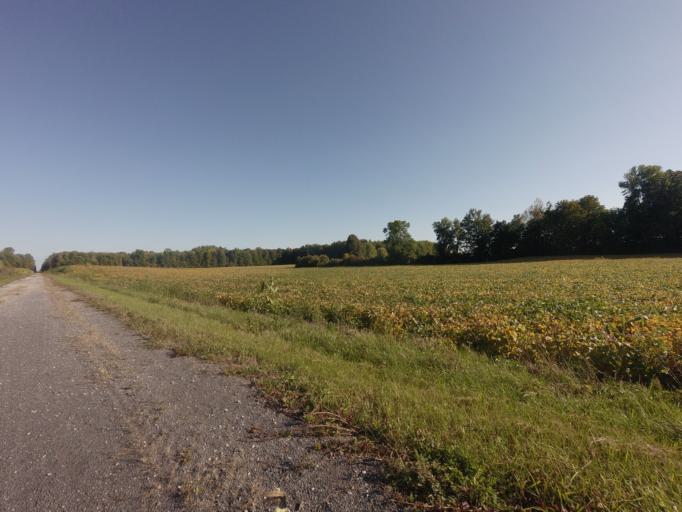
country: CA
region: Ontario
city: Hawkesbury
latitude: 45.5309
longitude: -74.5724
